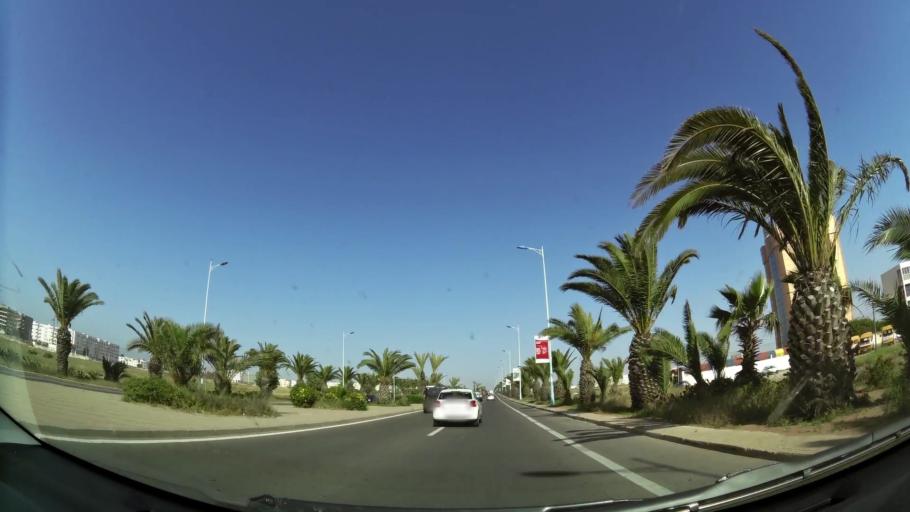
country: MA
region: Oued ed Dahab-Lagouira
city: Dakhla
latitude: 30.4034
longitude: -9.5681
